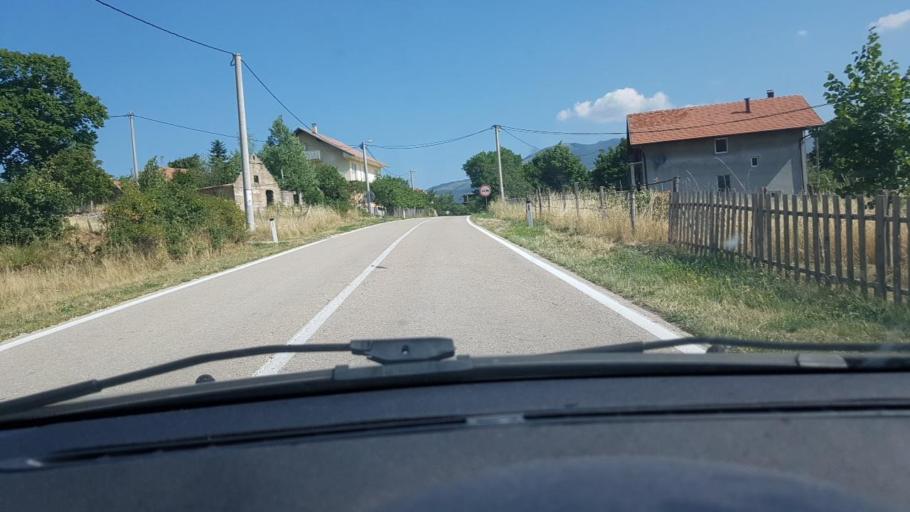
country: BA
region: Federation of Bosnia and Herzegovina
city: Bosansko Grahovo
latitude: 44.0773
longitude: 16.5711
